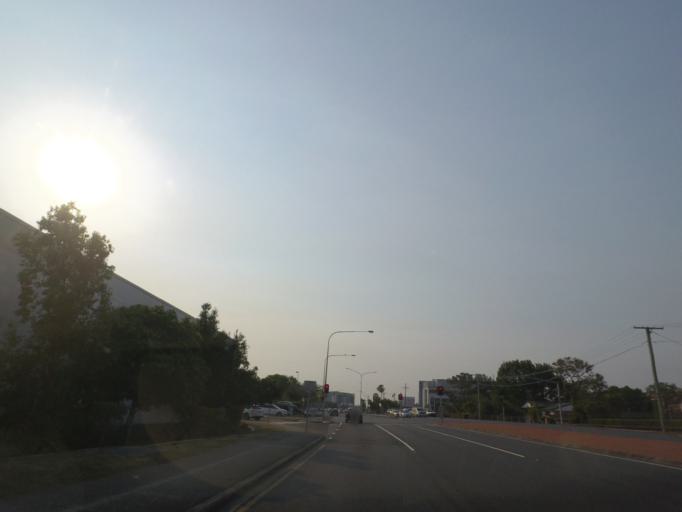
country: AU
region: Queensland
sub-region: Brisbane
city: Upper Mount Gravatt
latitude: -27.5629
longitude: 153.0854
